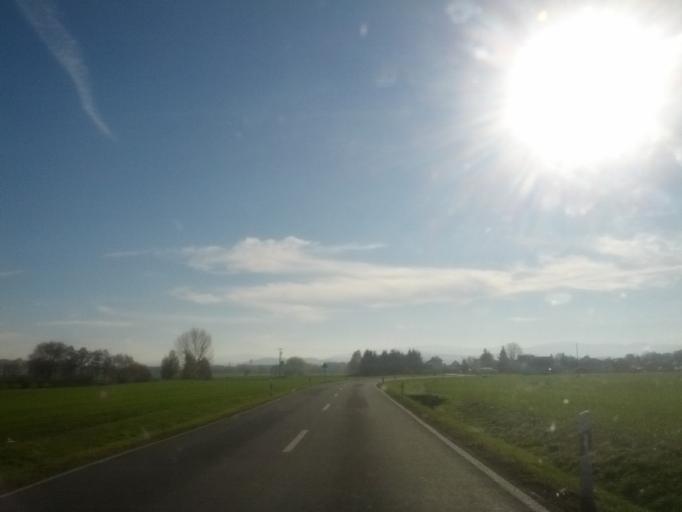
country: DE
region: Thuringia
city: Mechterstadt
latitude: 50.9340
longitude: 10.5480
